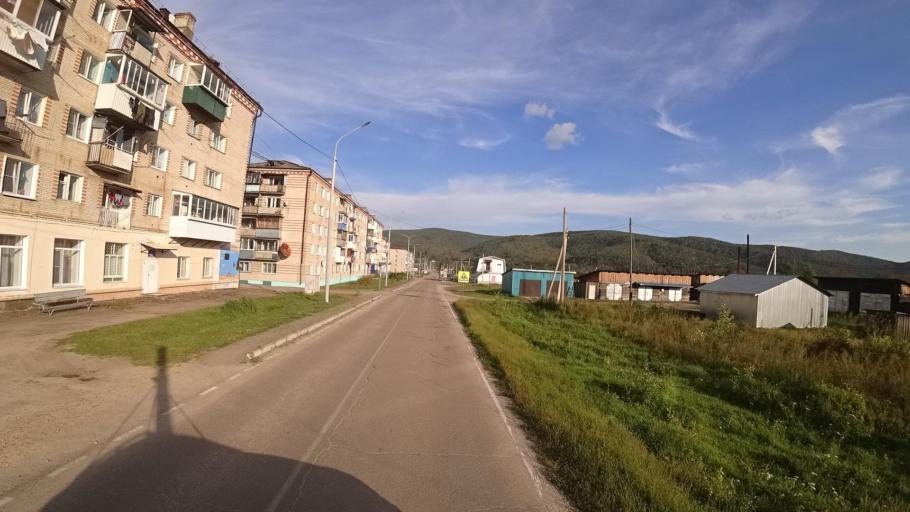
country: RU
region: Jewish Autonomous Oblast
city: Kul'dur
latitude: 49.2025
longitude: 131.6229
